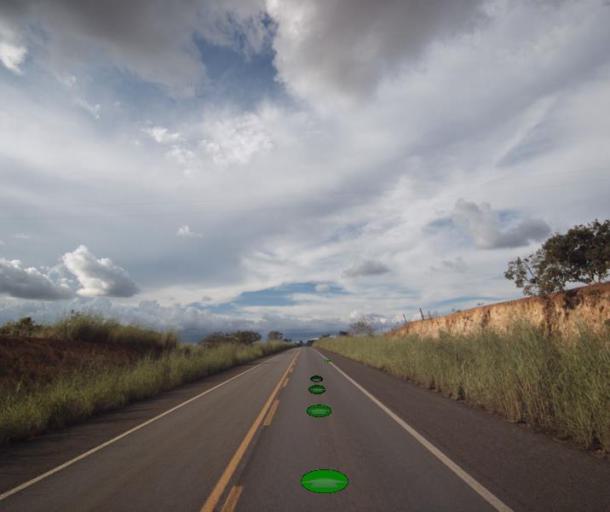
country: BR
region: Goias
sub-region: Niquelandia
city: Niquelandia
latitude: -14.7626
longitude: -48.6228
